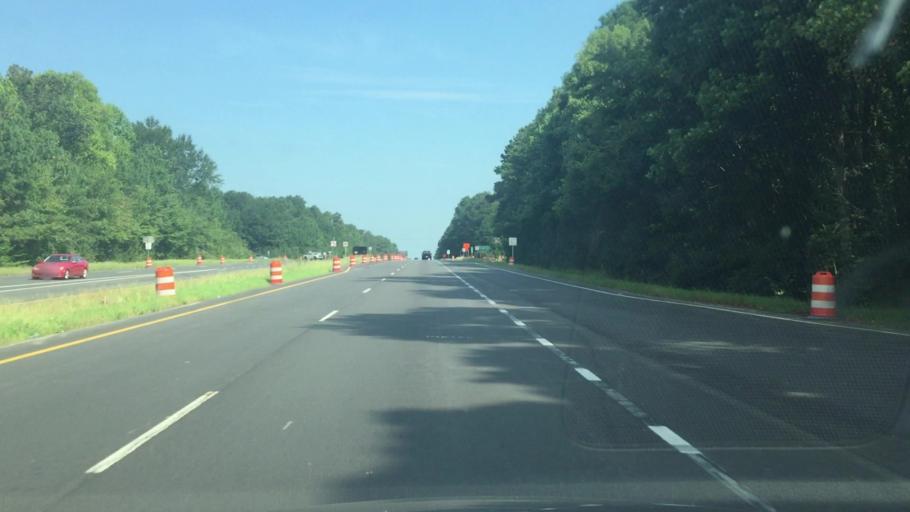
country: US
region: North Carolina
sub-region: Robeson County
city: Fairmont
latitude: 34.4790
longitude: -78.9870
